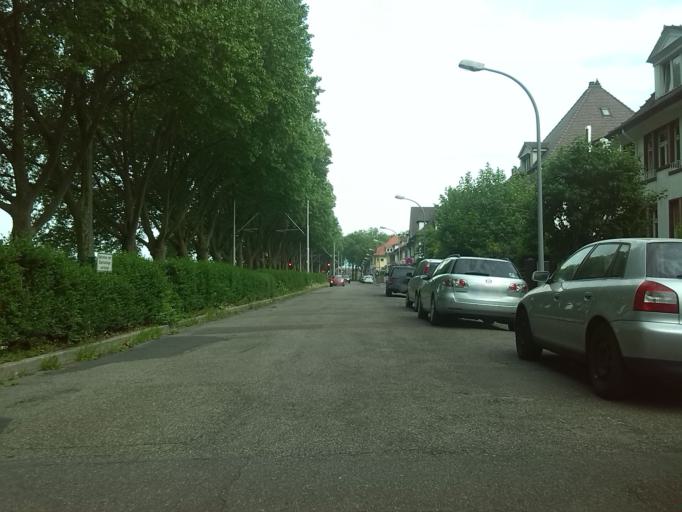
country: DE
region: Baden-Wuerttemberg
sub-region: Karlsruhe Region
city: Mannheim
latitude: 49.4798
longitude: 8.5172
